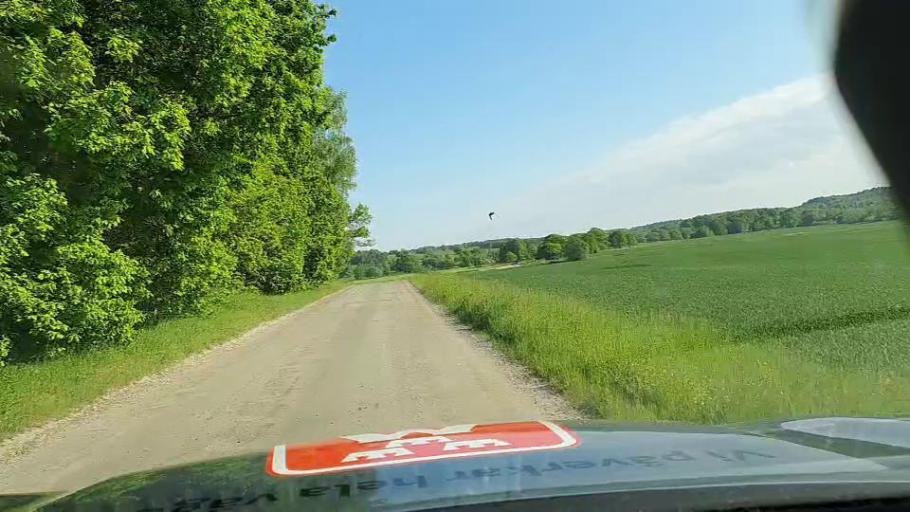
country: SE
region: Skane
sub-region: Hassleholms Kommun
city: Tormestorp
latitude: 56.1165
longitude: 13.7177
